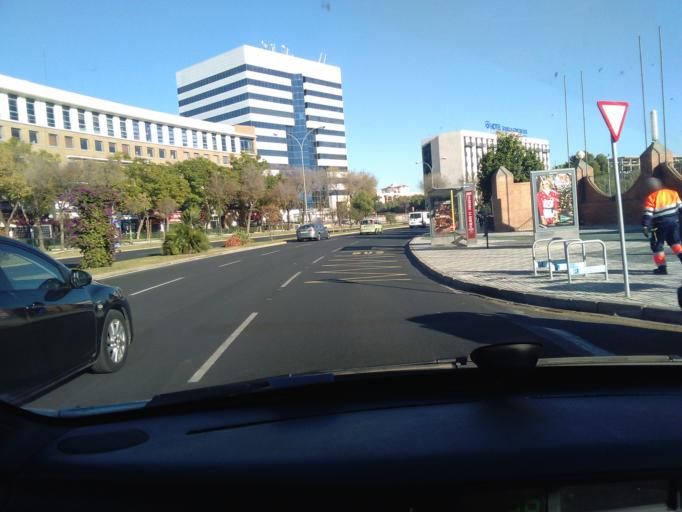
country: ES
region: Andalusia
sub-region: Provincia de Sevilla
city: Sevilla
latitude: 37.4055
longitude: -5.9325
